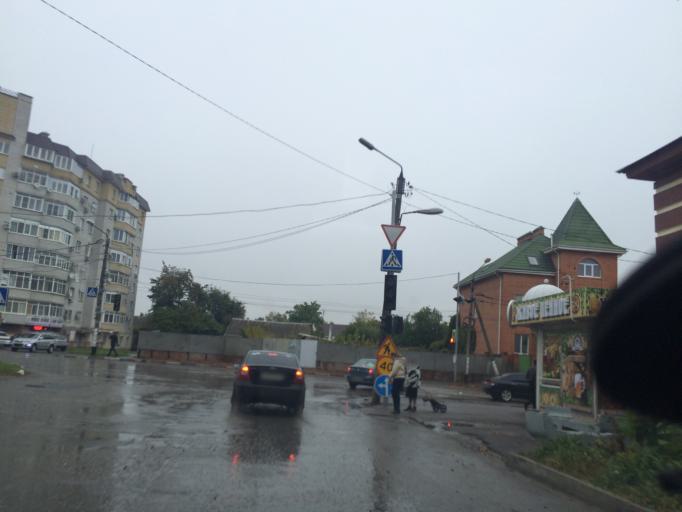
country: RU
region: Rostov
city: Azov
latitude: 47.1058
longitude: 39.4315
